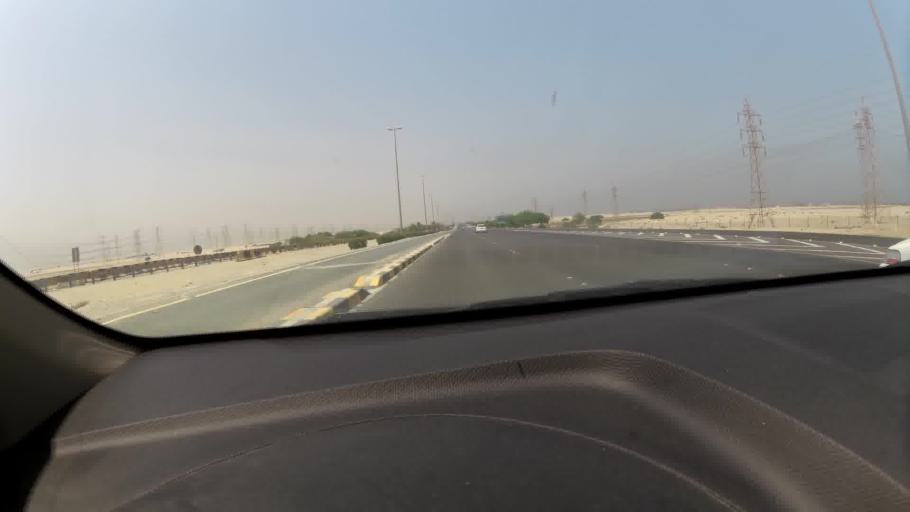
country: KW
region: Al Ahmadi
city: Al Fahahil
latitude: 28.8661
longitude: 48.2368
